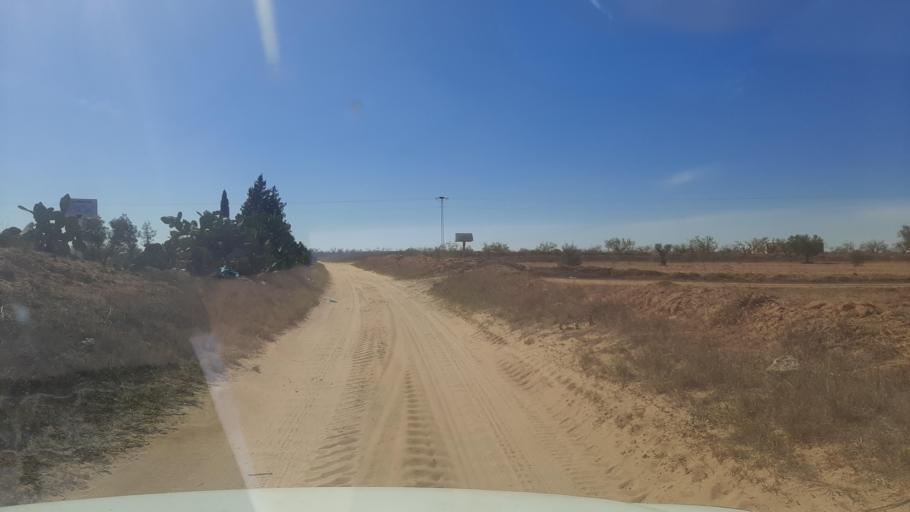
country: TN
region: Safaqis
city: Sfax
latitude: 34.8298
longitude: 10.5560
